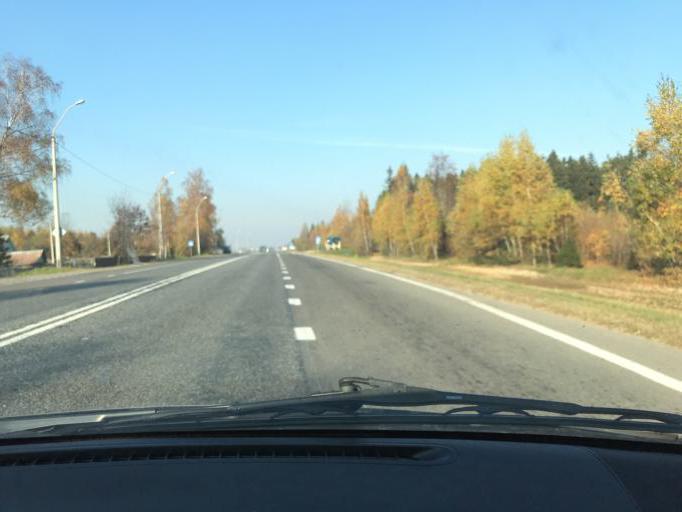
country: BY
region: Vitebsk
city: Orsha
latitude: 54.3919
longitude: 30.4433
